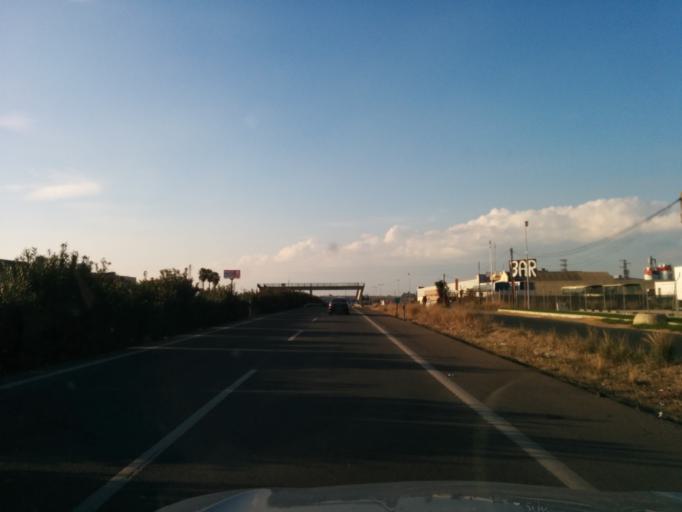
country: ES
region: Andalusia
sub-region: Provincia de Sevilla
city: Dos Hermanas
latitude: 37.3114
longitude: -5.8919
